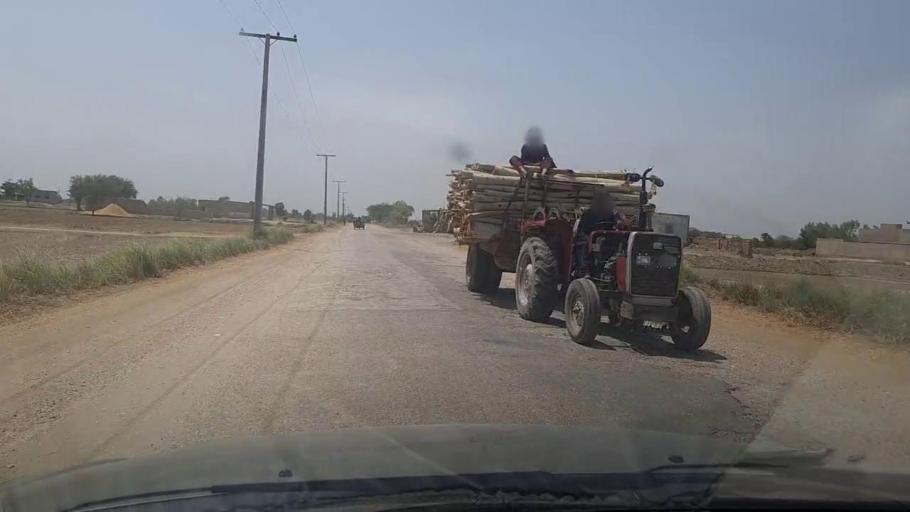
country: PK
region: Sindh
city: Bhiria
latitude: 26.8928
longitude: 68.2494
